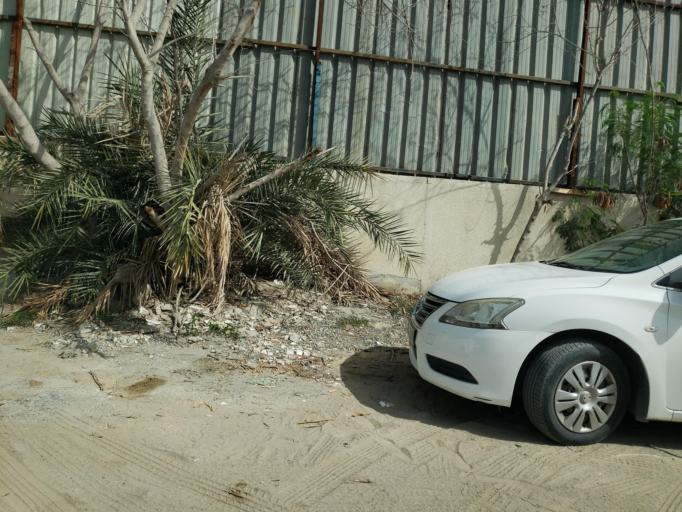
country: AE
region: Ash Shariqah
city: Sharjah
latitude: 25.3358
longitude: 55.4044
